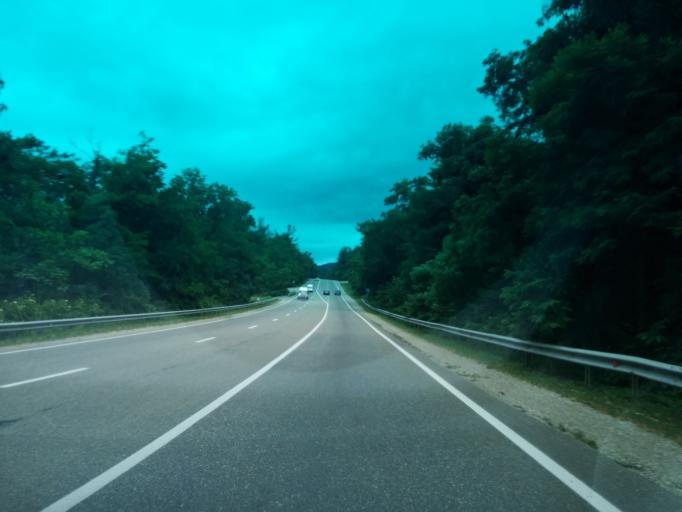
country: RU
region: Krasnodarskiy
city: Ol'ginka
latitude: 44.1783
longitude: 38.9407
